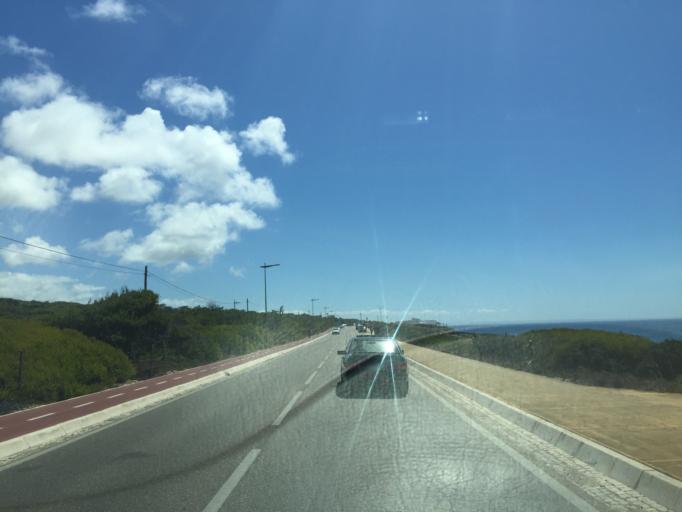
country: PT
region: Lisbon
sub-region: Cascais
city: Cascais
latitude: 38.7026
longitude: -9.4749
